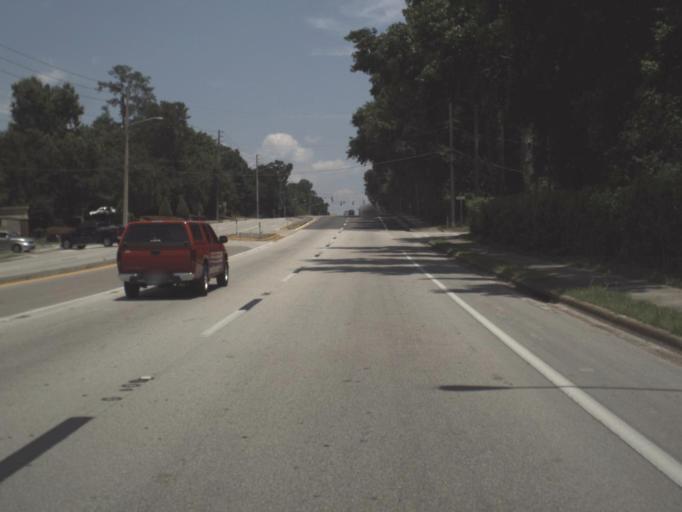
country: US
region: Florida
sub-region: Alachua County
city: Gainesville
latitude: 29.6568
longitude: -82.3933
